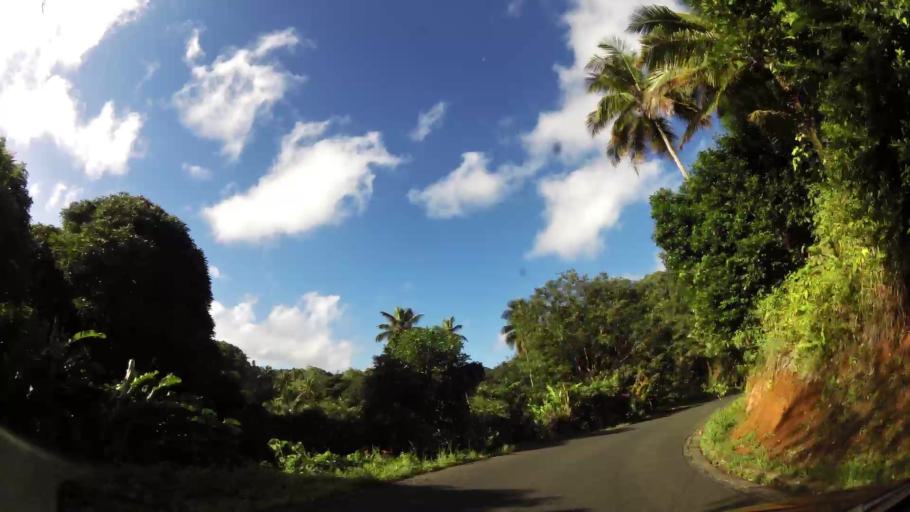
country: DM
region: Saint Andrew
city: Calibishie
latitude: 15.5873
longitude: -61.4021
